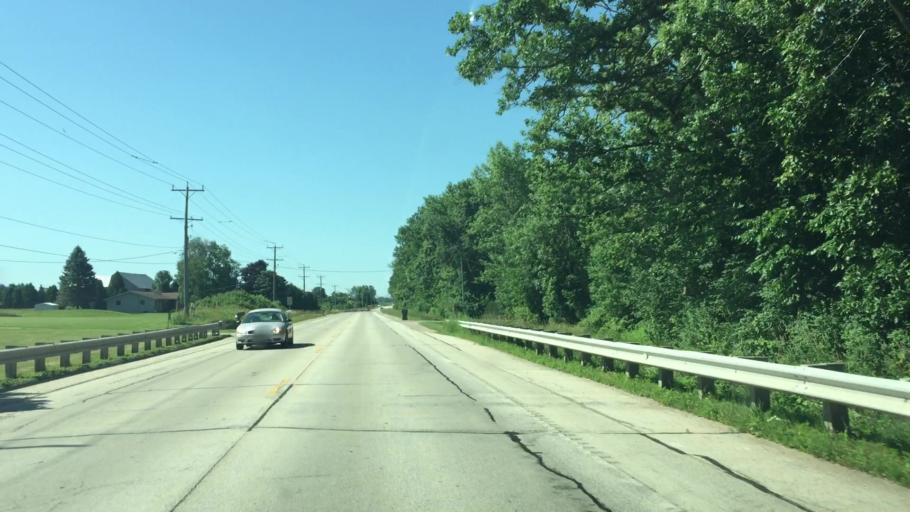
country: US
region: Wisconsin
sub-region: Calumet County
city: Sherwood
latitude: 44.1584
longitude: -88.2649
